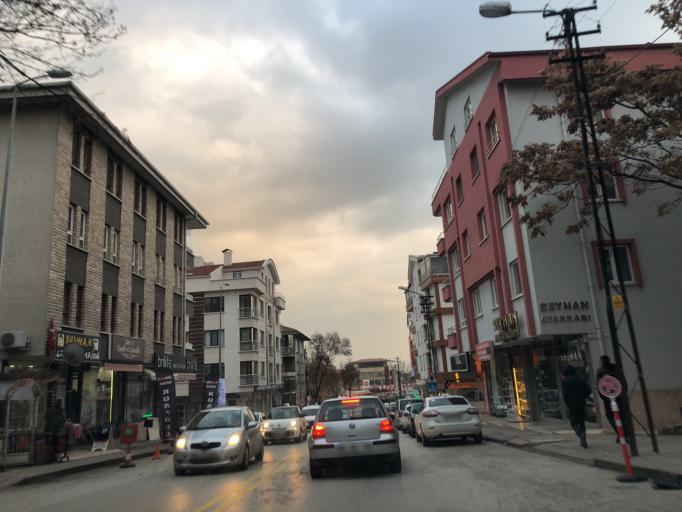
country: TR
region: Ankara
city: Ankara
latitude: 39.9679
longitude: 32.8081
